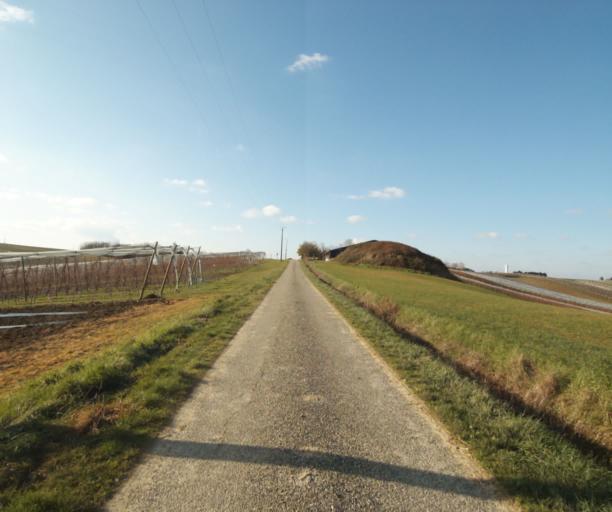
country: FR
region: Midi-Pyrenees
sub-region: Departement du Tarn-et-Garonne
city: Saint-Nicolas-de-la-Grave
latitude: 44.1249
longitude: 1.0272
